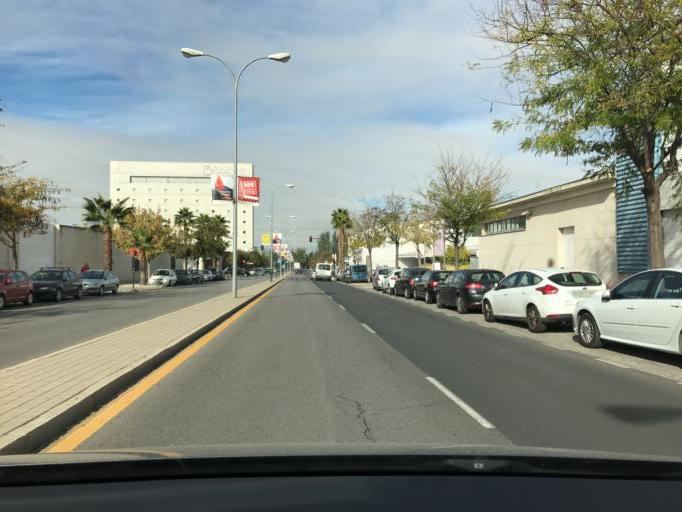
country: ES
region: Andalusia
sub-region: Provincia de Granada
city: Armilla
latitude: 37.1616
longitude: -3.6055
